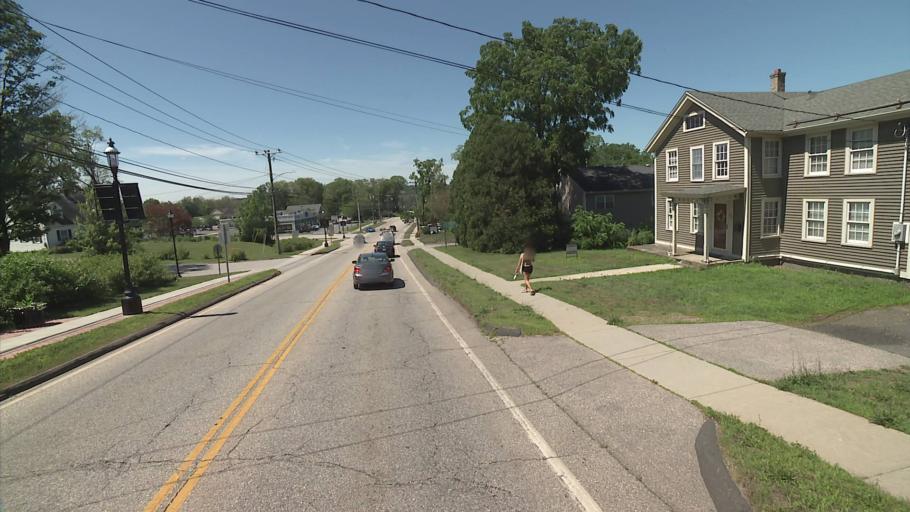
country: US
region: Connecticut
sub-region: New London County
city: Colchester
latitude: 41.5737
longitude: -72.3338
